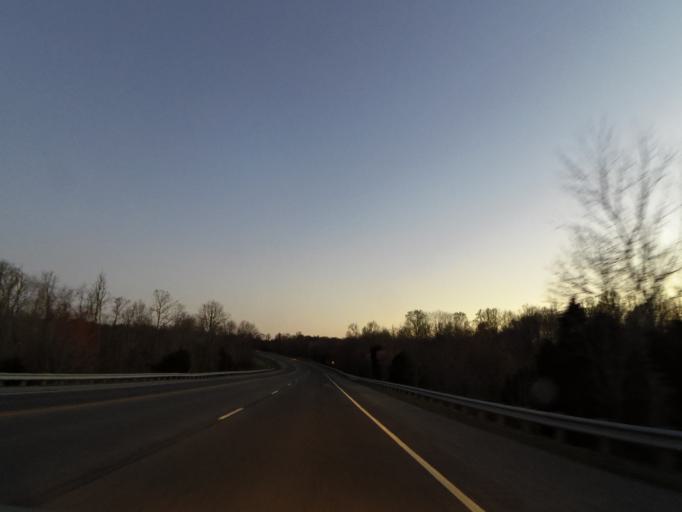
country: US
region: Tennessee
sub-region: Robertson County
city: Springfield
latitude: 36.4577
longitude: -86.8974
